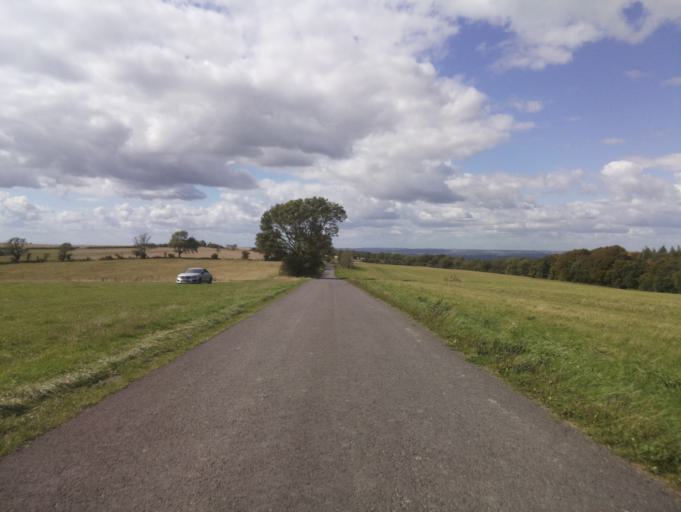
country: GB
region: England
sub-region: Wiltshire
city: Erlestoke
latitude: 51.2731
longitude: -2.0651
